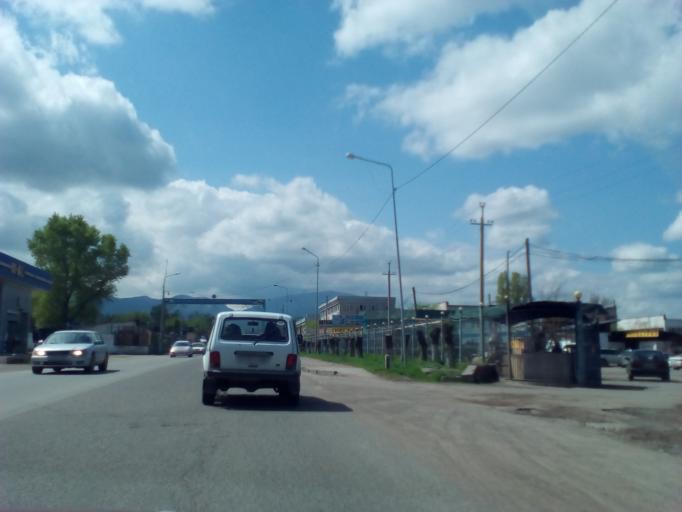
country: KZ
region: Almaty Oblysy
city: Burunday
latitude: 43.2143
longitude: 76.6443
